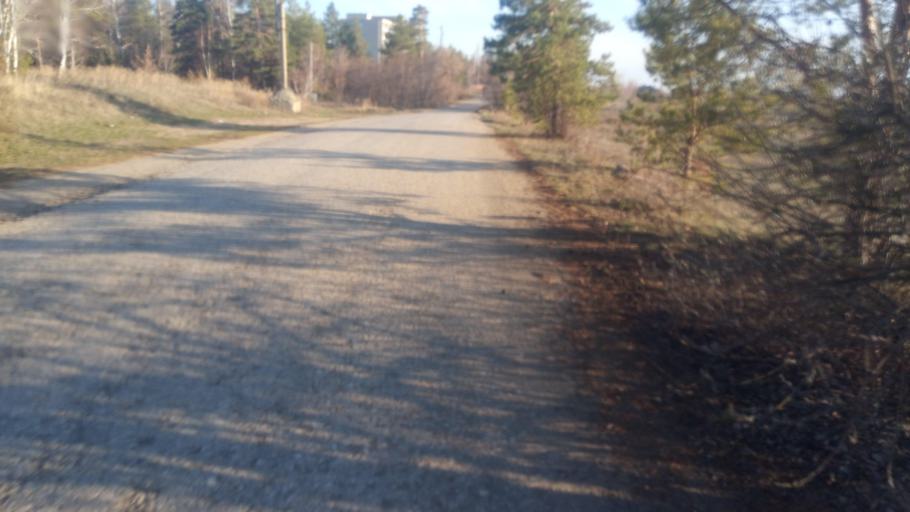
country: RU
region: Chelyabinsk
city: Novosineglazovskiy
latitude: 55.1267
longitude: 61.3286
